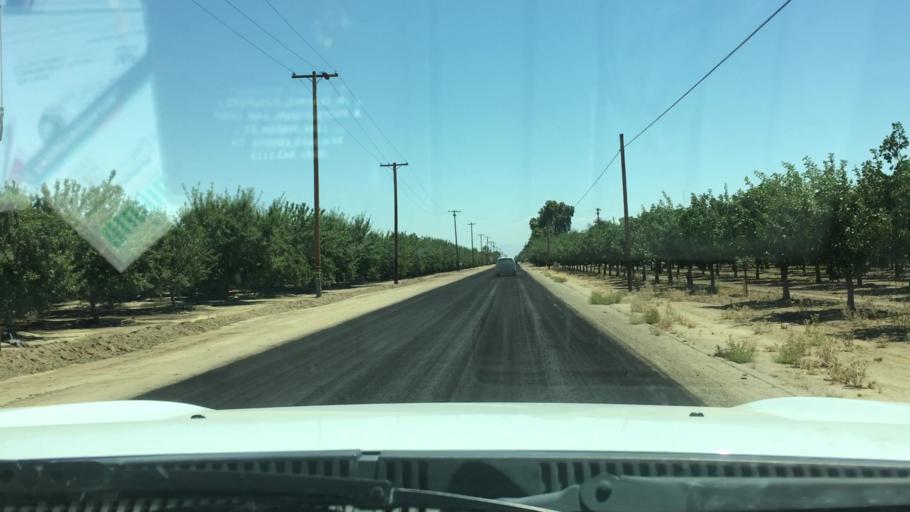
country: US
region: California
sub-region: Kern County
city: Wasco
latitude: 35.5290
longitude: -119.3312
